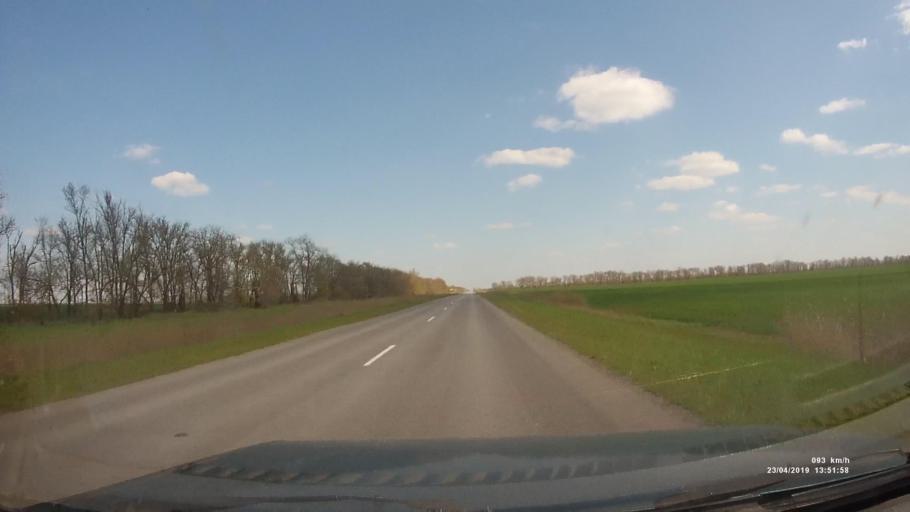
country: RU
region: Rostov
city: Remontnoye
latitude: 46.6003
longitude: 42.9450
